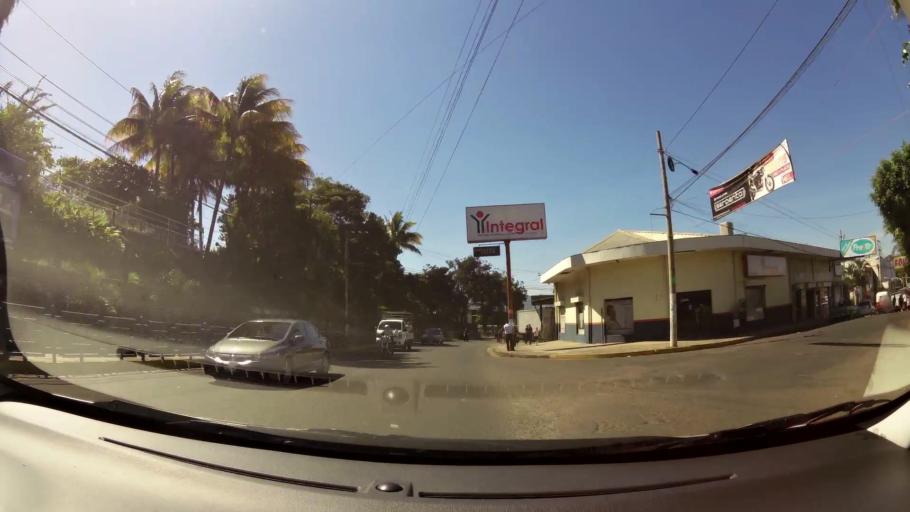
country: SV
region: Ahuachapan
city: Ahuachapan
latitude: 13.9237
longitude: -89.8438
